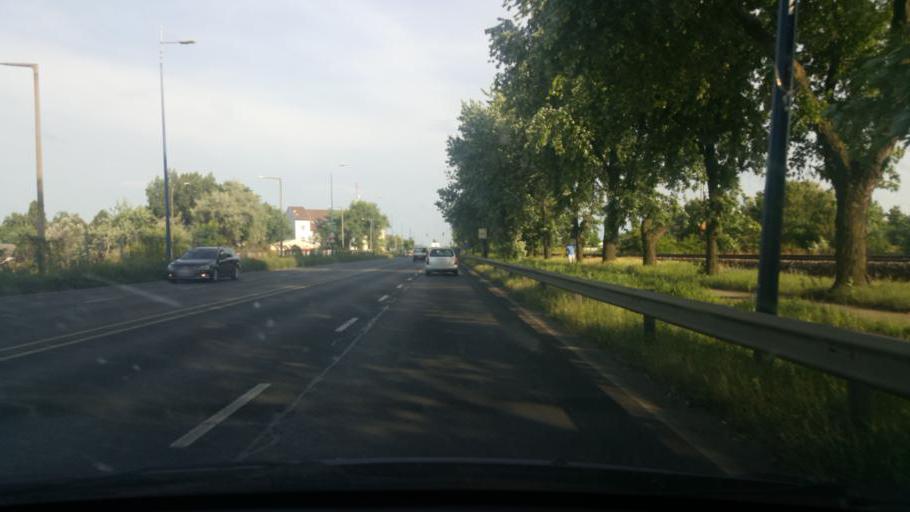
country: HU
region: Pest
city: Gyal
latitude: 47.4254
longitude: 19.2376
